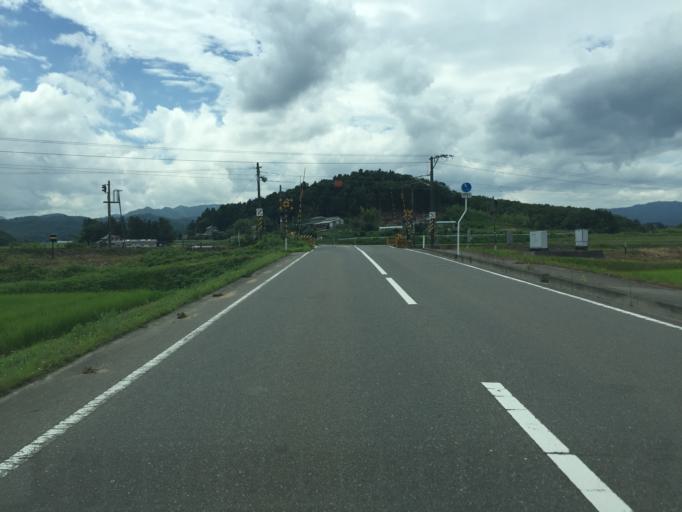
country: JP
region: Miyagi
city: Marumori
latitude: 37.7595
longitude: 140.9324
